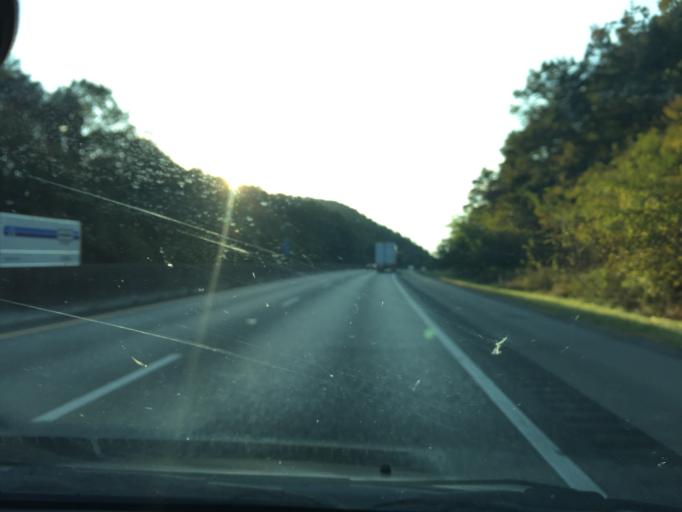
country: US
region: Tennessee
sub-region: Hamilton County
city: Collegedale
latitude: 35.1271
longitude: -85.0185
